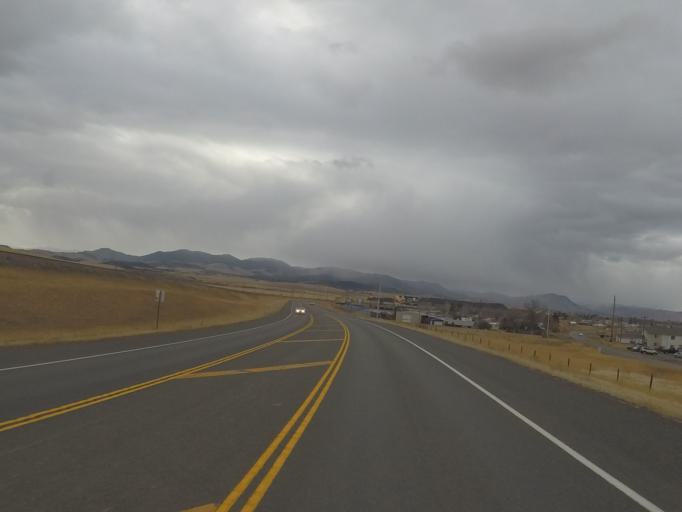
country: US
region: Montana
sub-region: Lewis and Clark County
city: East Helena
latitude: 46.5876
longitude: -111.8905
